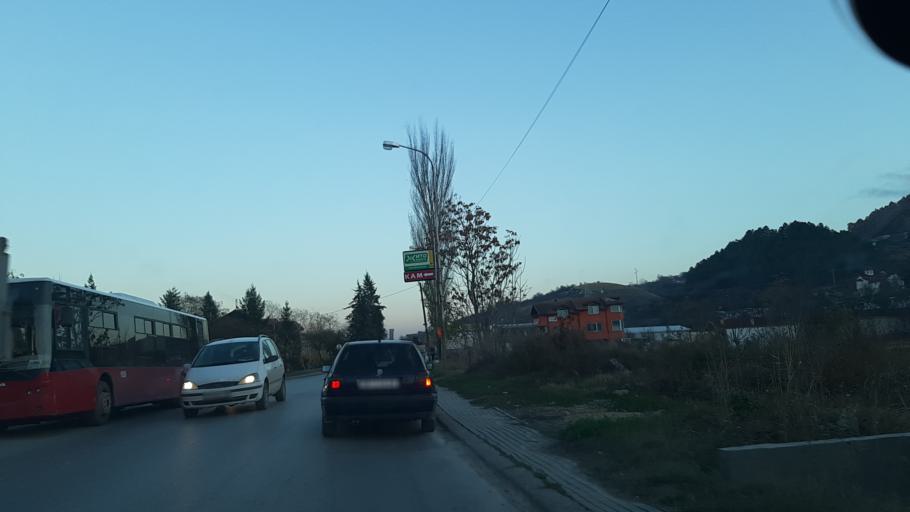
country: MK
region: Kisela Voda
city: Kisela Voda
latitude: 41.9382
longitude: 21.5088
